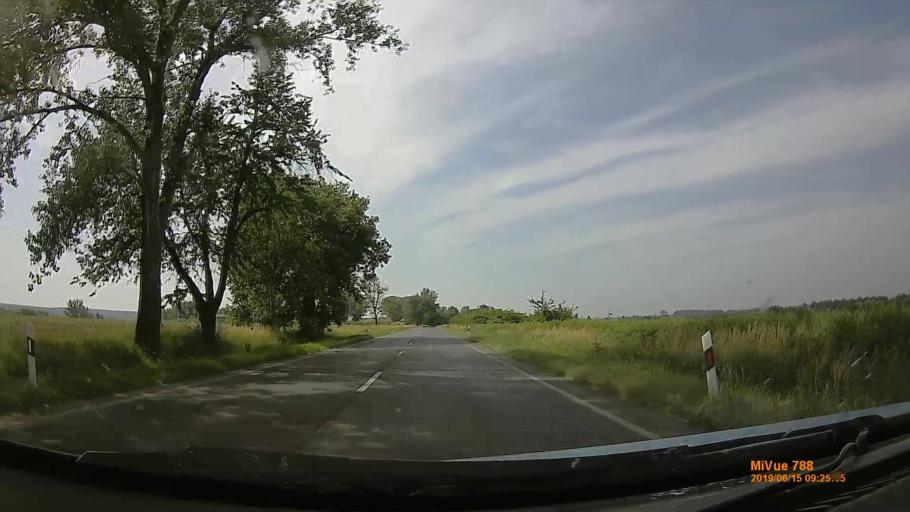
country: HU
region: Tolna
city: Dobrokoz
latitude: 46.5418
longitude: 18.1709
